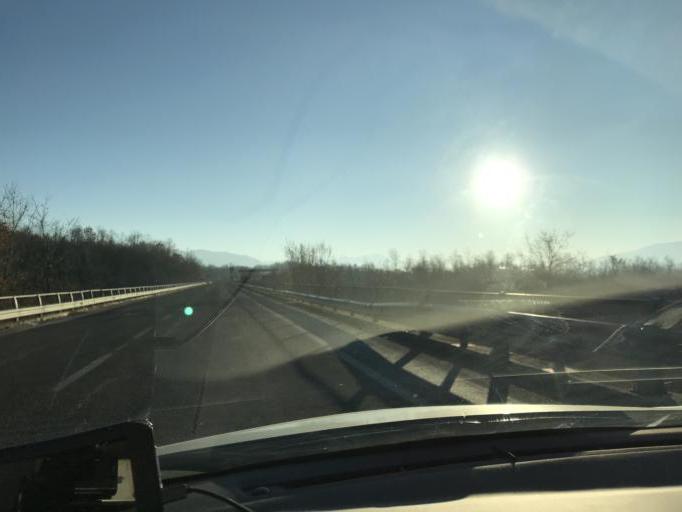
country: IT
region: Latium
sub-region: Provincia di Rieti
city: Fiamignano
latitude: 42.2621
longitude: 13.0892
